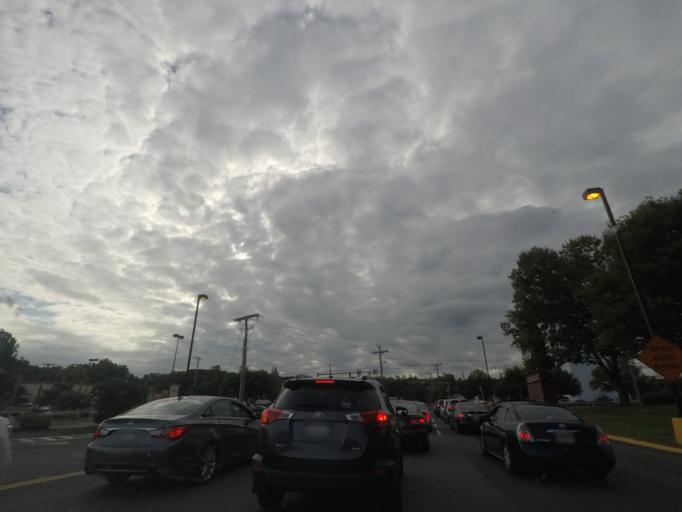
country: US
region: Massachusetts
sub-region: Hampden County
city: West Springfield
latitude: 42.1294
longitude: -72.6255
